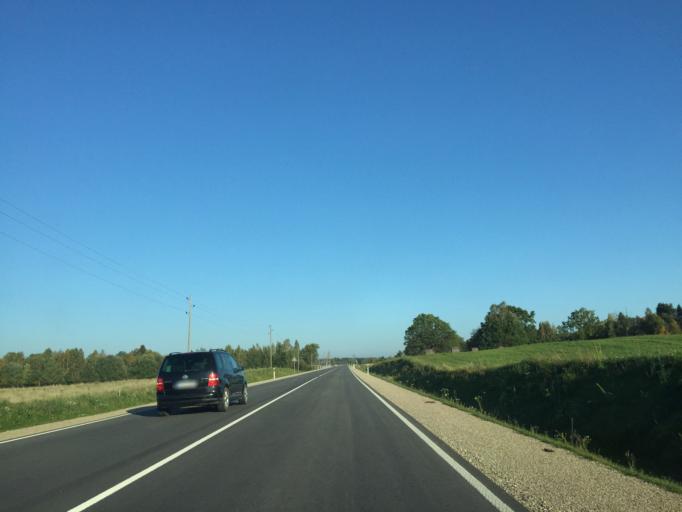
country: LV
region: Vecpiebalga
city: Vecpiebalga
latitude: 57.0892
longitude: 25.7395
